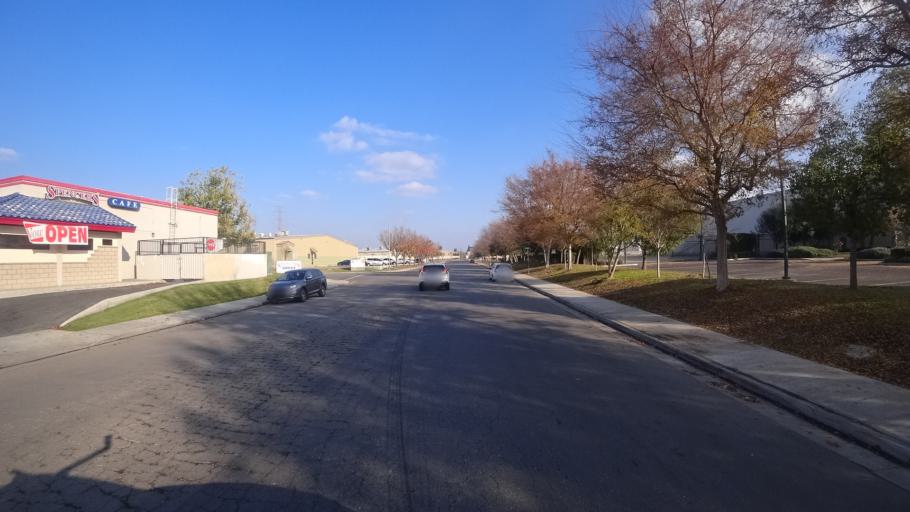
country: US
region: California
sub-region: Kern County
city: Greenacres
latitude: 35.3167
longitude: -119.0900
